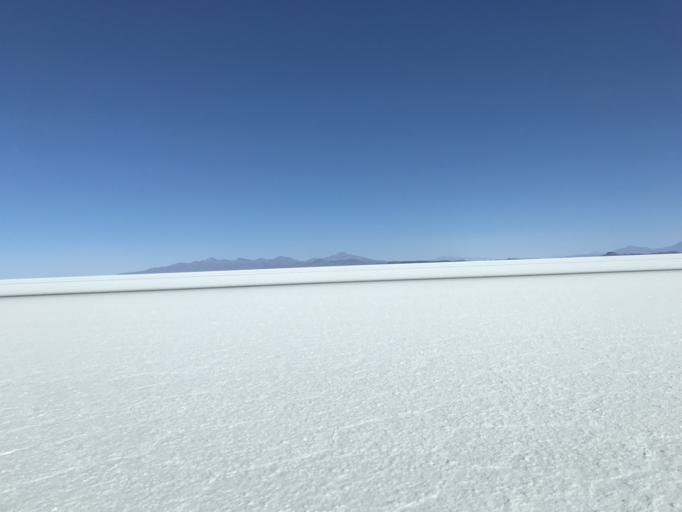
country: BO
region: Potosi
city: Colchani
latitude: -20.2401
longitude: -67.6117
